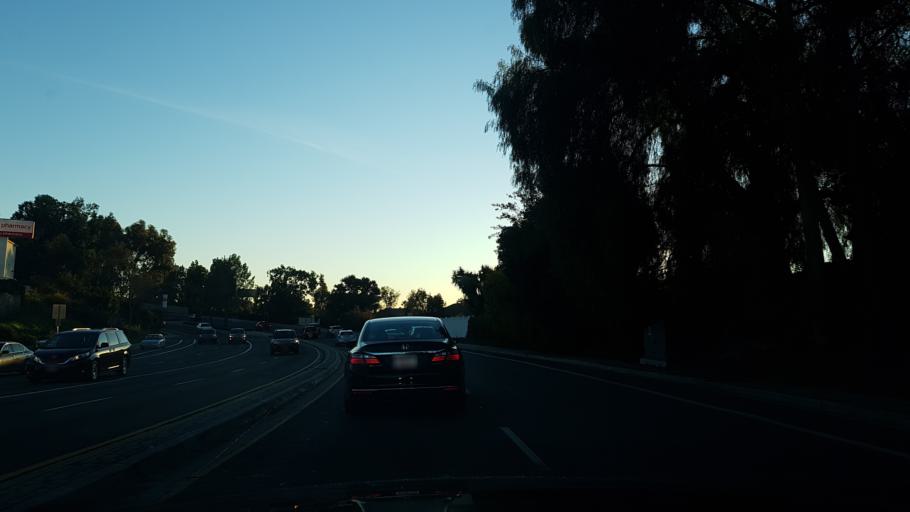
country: US
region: California
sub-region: San Diego County
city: Fairbanks Ranch
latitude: 32.9573
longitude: -117.1287
